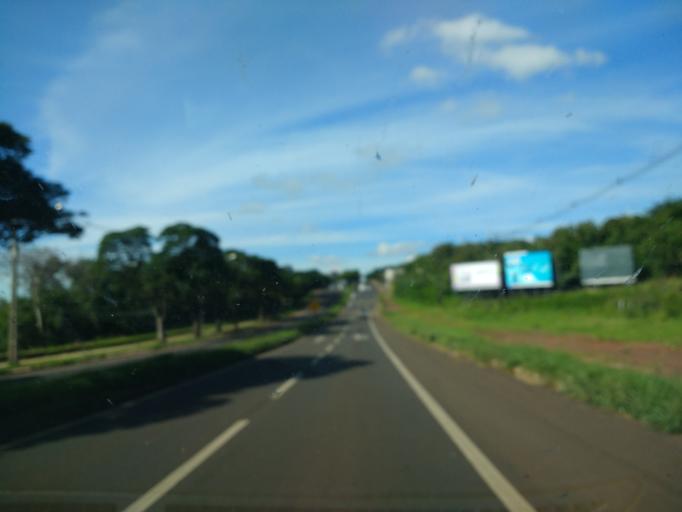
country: BR
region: Parana
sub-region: Maringa
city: Maringa
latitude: -23.4187
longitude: -51.9629
